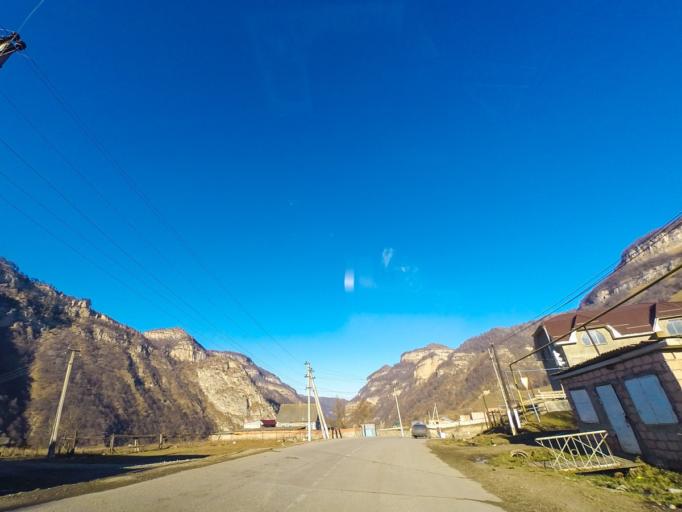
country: RU
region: Kabardino-Balkariya
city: Zhankhoteko
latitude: 43.4371
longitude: 43.2374
